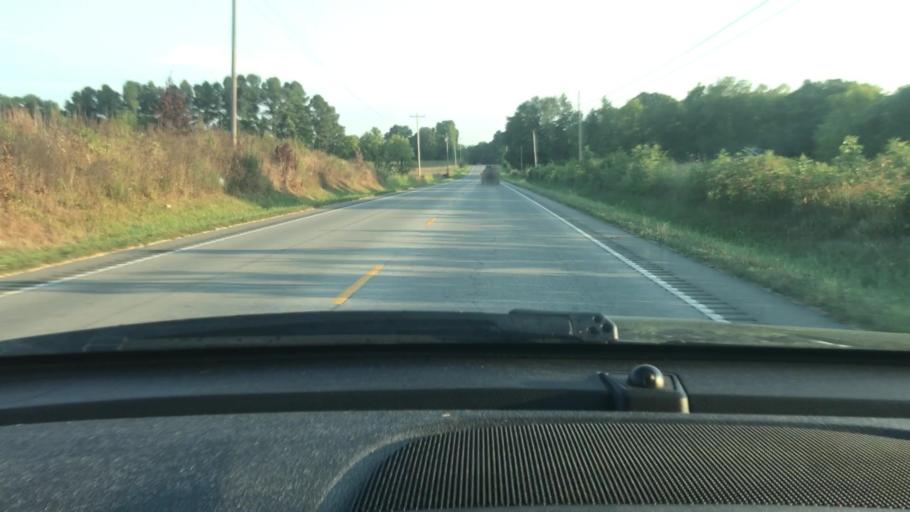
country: US
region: Tennessee
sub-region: Dickson County
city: Charlotte
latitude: 36.1456
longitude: -87.3567
